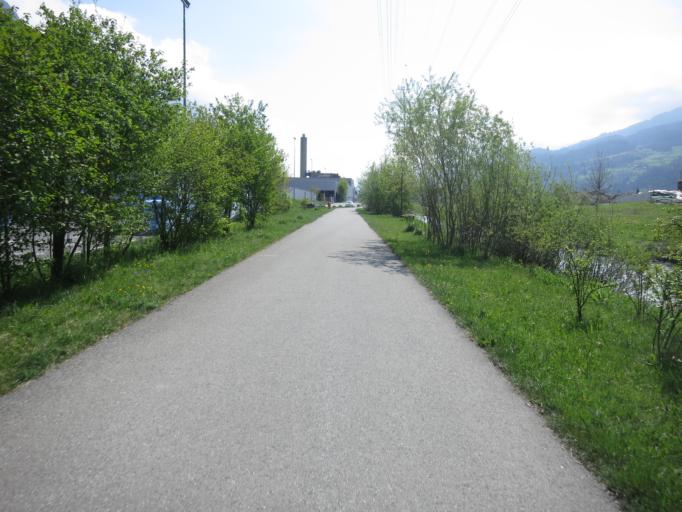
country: CH
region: Saint Gallen
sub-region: Wahlkreis Sarganserland
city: Flums
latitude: 47.1013
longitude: 9.3406
